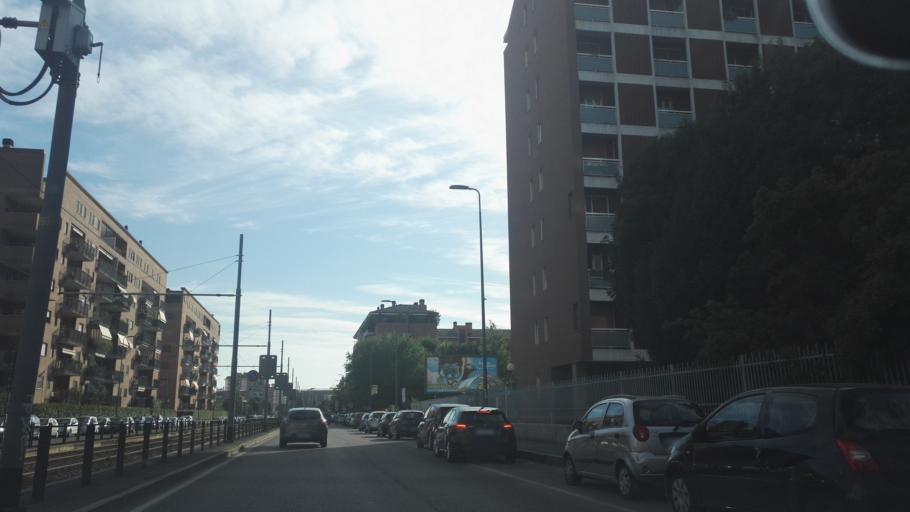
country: IT
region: Lombardy
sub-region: Citta metropolitana di Milano
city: Romano Banco
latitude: 45.4438
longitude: 9.1272
